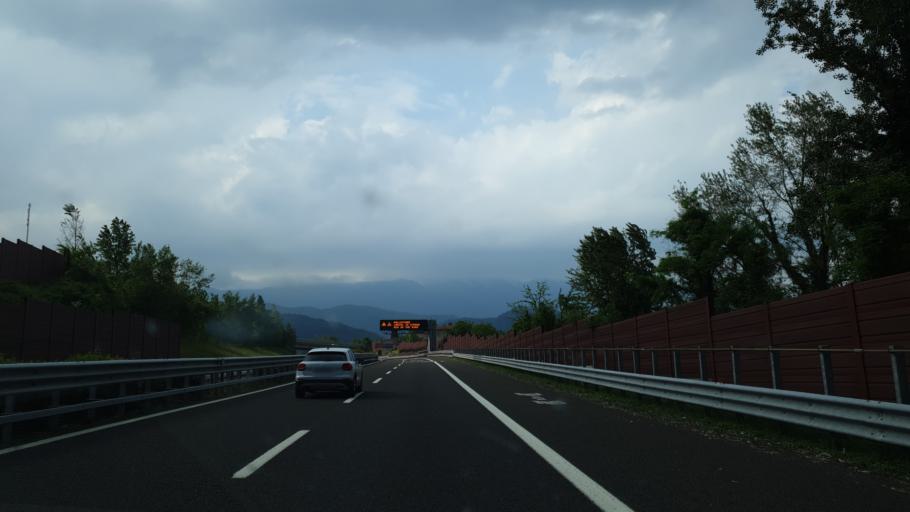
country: IT
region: Veneto
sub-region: Provincia di Treviso
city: Carpesica
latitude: 45.9558
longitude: 12.2922
